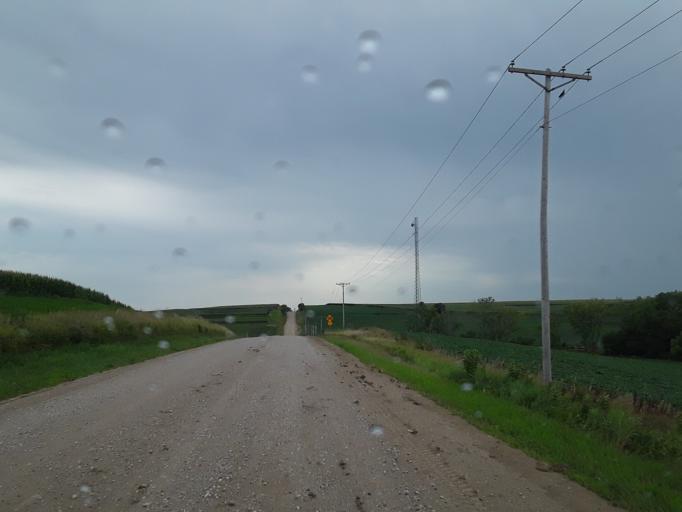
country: US
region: Nebraska
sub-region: Washington County
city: Blair
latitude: 41.5092
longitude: -96.1703
